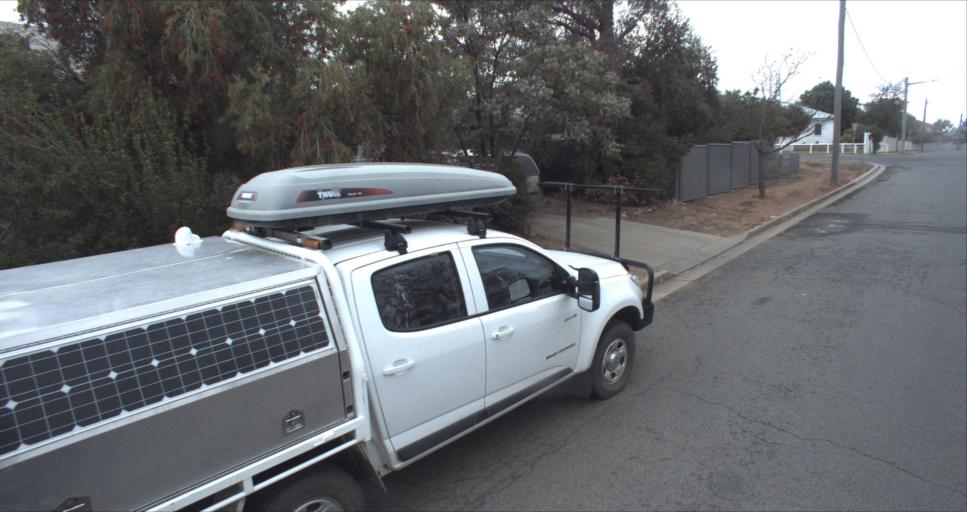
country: AU
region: New South Wales
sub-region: Leeton
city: Leeton
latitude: -34.5499
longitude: 146.4014
